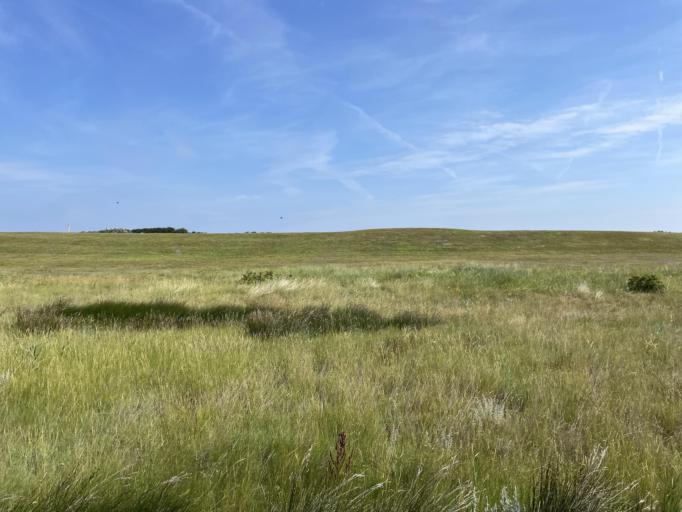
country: DE
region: Lower Saxony
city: Wangerooge
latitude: 53.7882
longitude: 7.8821
